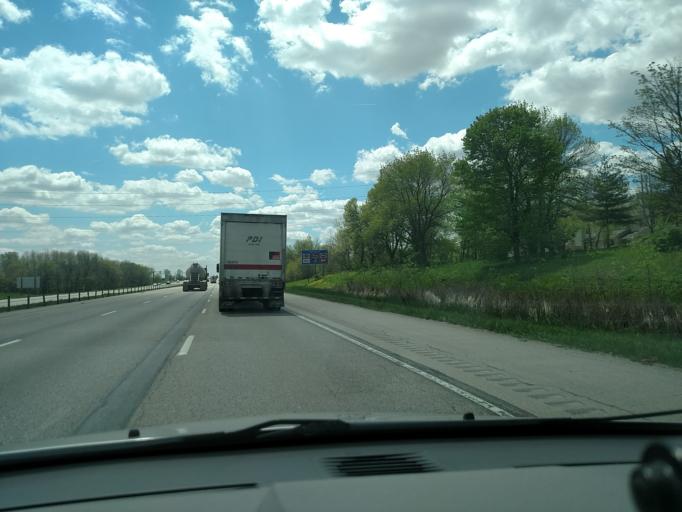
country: US
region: Iowa
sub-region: Polk County
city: Ankeny
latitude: 41.7188
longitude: -93.5766
